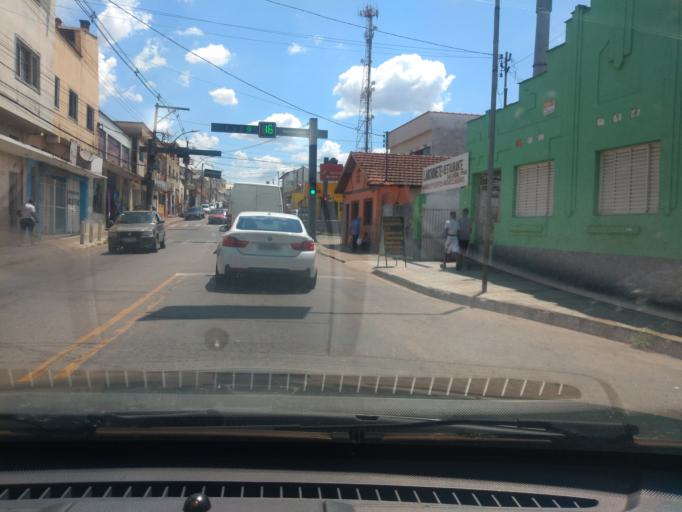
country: BR
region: Minas Gerais
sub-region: Tres Coracoes
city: Tres Coracoes
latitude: -21.6928
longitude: -45.2485
